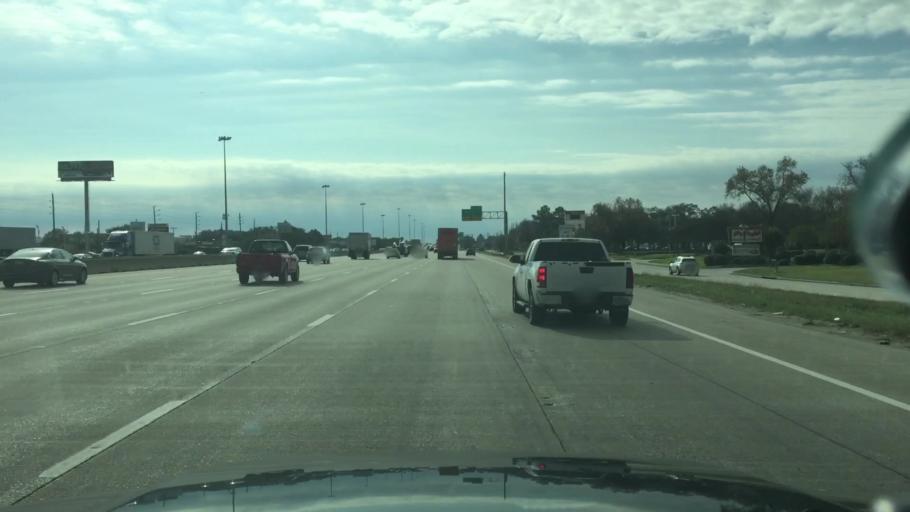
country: US
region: Texas
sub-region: Harris County
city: Aldine
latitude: 29.9915
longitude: -95.4246
